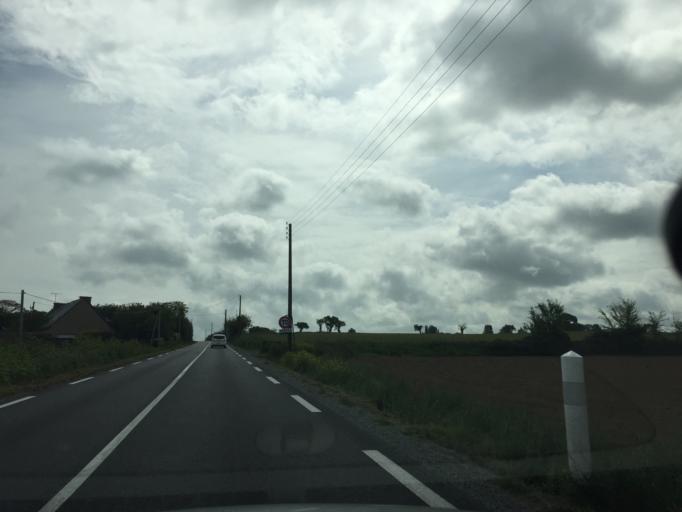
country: FR
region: Brittany
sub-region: Departement des Cotes-d'Armor
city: Crehen
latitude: 48.5669
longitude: -2.2050
